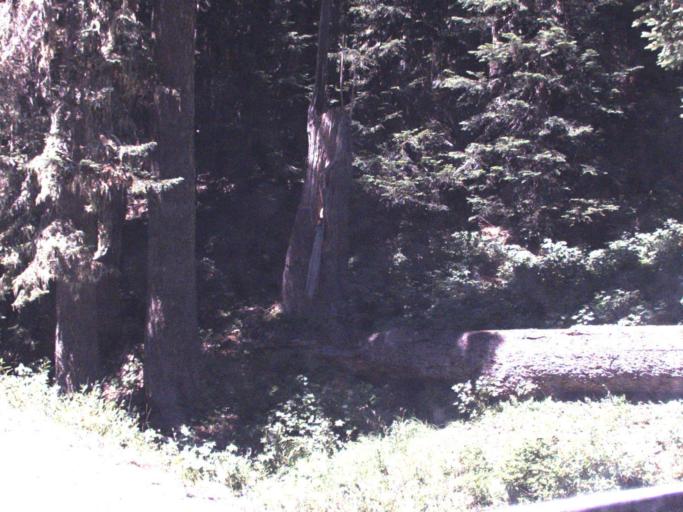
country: US
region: Washington
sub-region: King County
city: Enumclaw
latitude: 46.8555
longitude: -121.5165
